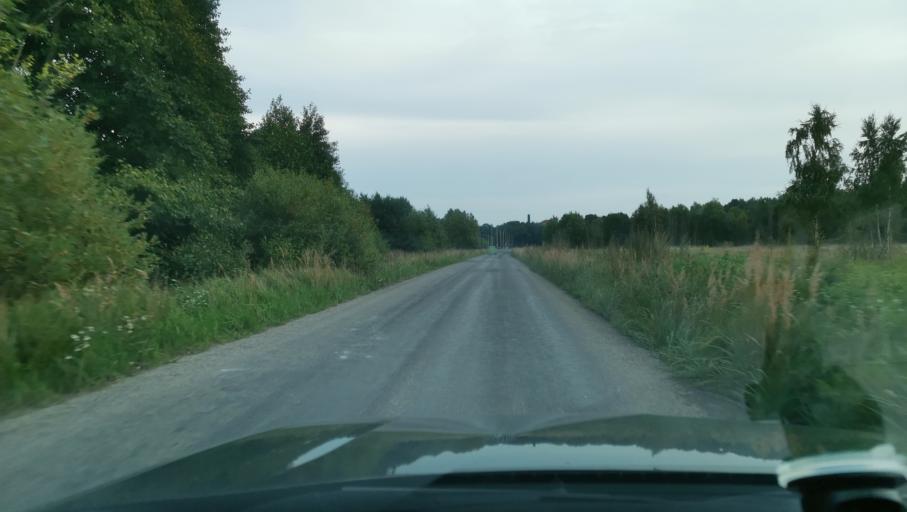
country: EE
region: Harju
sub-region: Saue vald
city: Laagri
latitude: 59.4215
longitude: 24.6274
